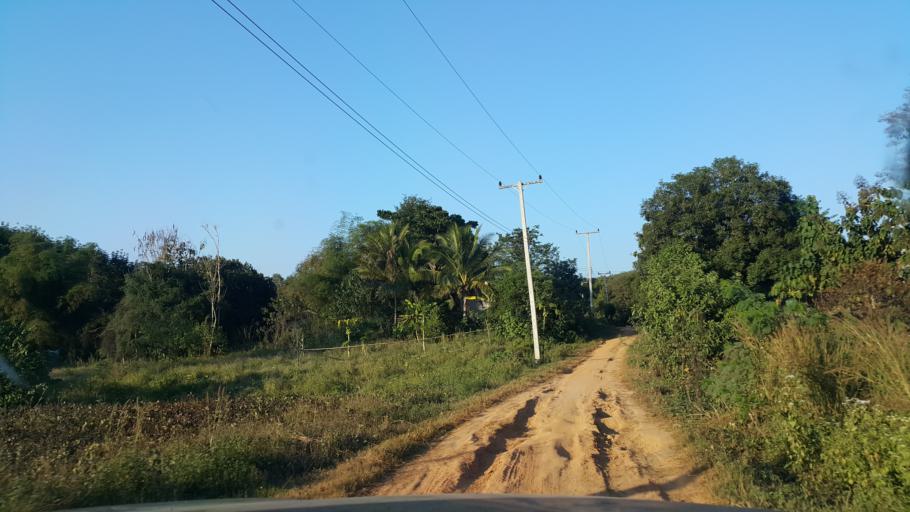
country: TH
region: Sukhothai
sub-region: Amphoe Si Satchanalai
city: Si Satchanalai
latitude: 17.5907
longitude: 99.6154
